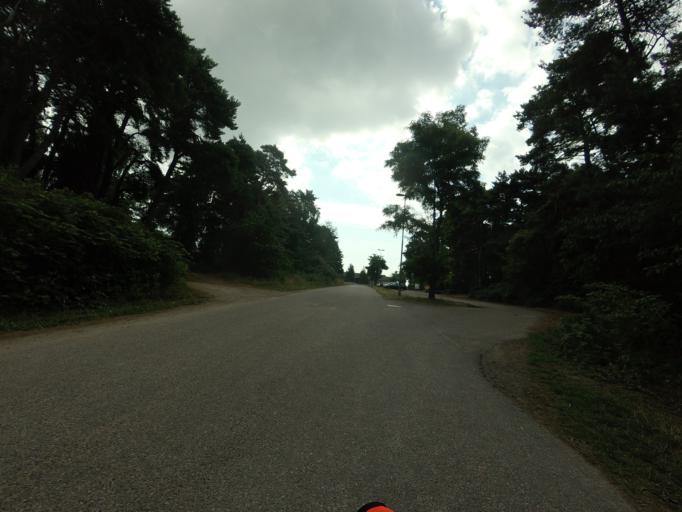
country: SE
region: Skane
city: Smygehamn
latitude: 55.3639
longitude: 13.4323
